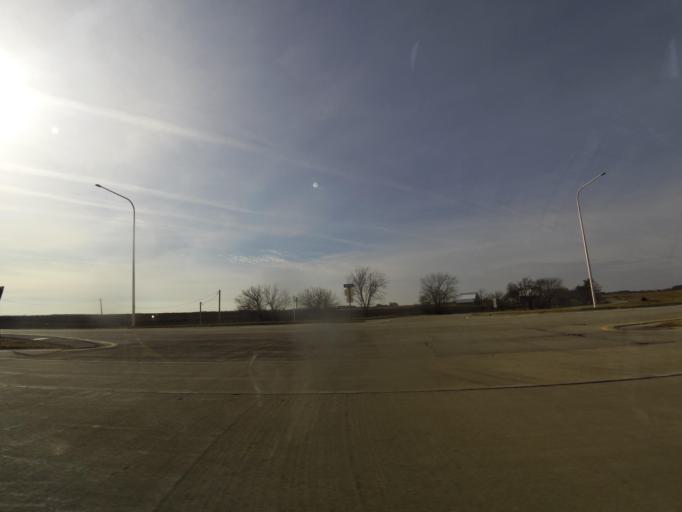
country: US
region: Illinois
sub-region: McLean County
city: Heyworth
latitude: 40.2976
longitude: -88.9795
